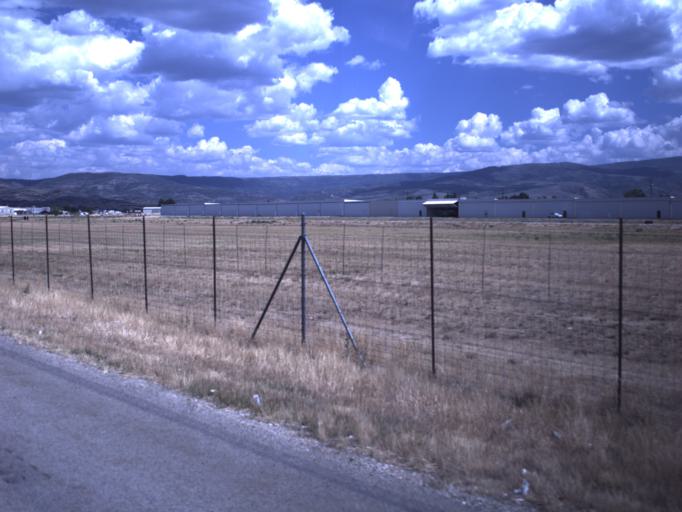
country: US
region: Utah
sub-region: Wasatch County
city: Heber
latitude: 40.4855
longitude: -111.4248
